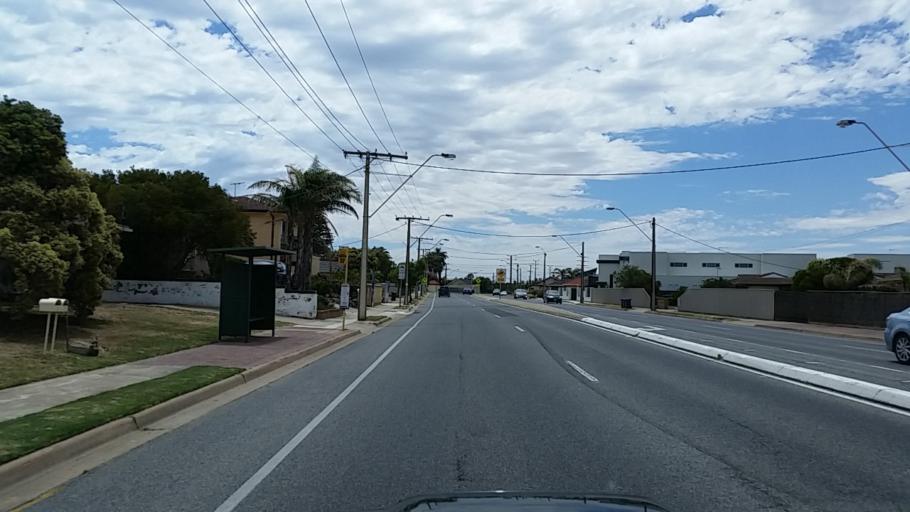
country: AU
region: South Australia
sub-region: Charles Sturt
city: West Lakes Shore
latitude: -34.8589
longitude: 138.4787
